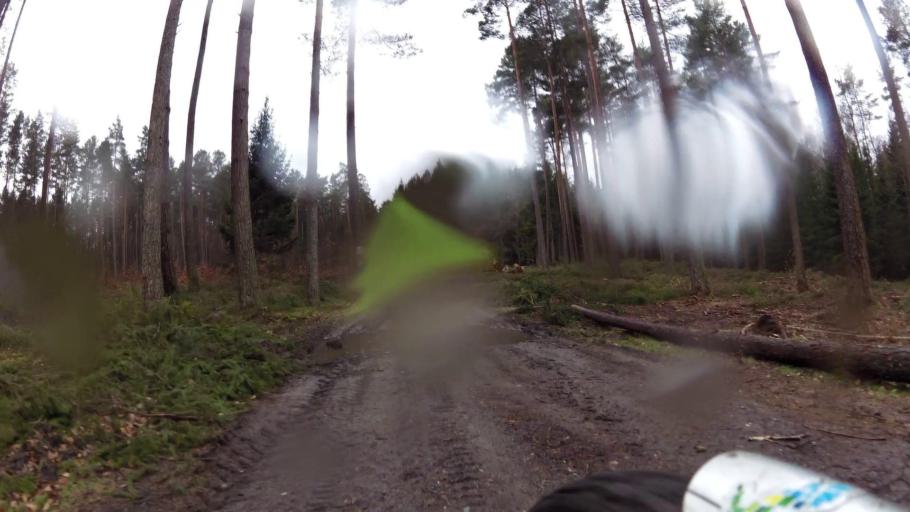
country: PL
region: Pomeranian Voivodeship
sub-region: Powiat bytowski
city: Miastko
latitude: 54.0695
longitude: 17.0820
